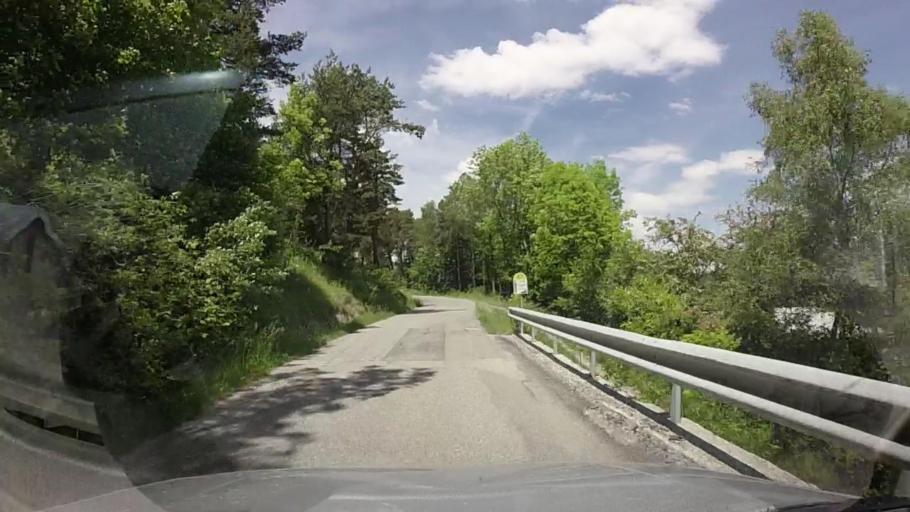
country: FR
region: Provence-Alpes-Cote d'Azur
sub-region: Departement des Alpes-de-Haute-Provence
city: Seyne-les-Alpes
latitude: 44.3333
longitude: 6.3480
